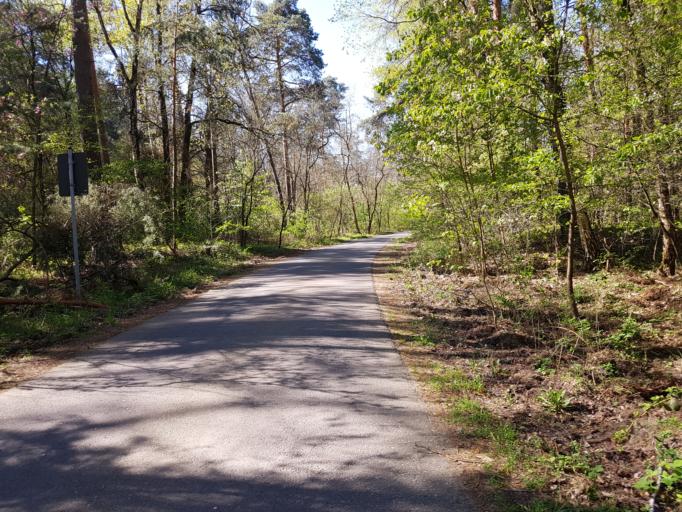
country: DE
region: Brandenburg
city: Groden
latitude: 51.3972
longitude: 13.5627
